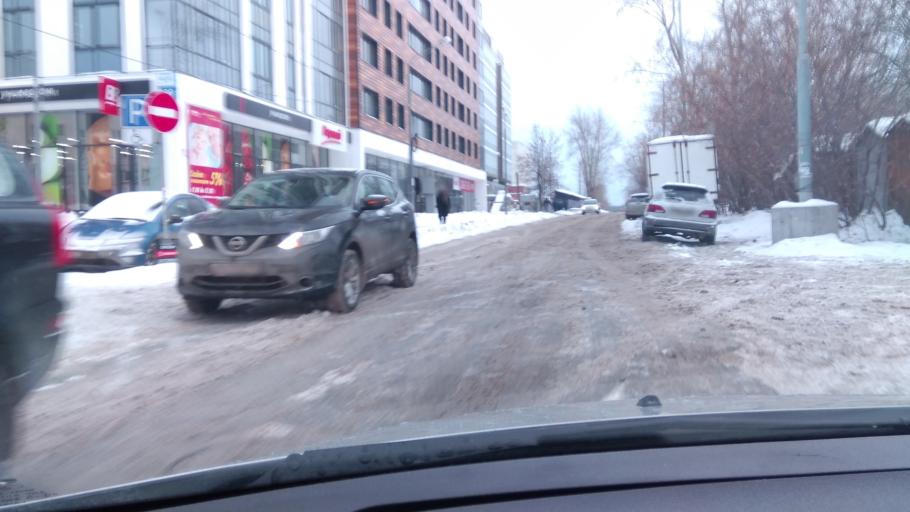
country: RU
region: Sverdlovsk
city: Yekaterinburg
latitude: 56.8070
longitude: 60.5959
